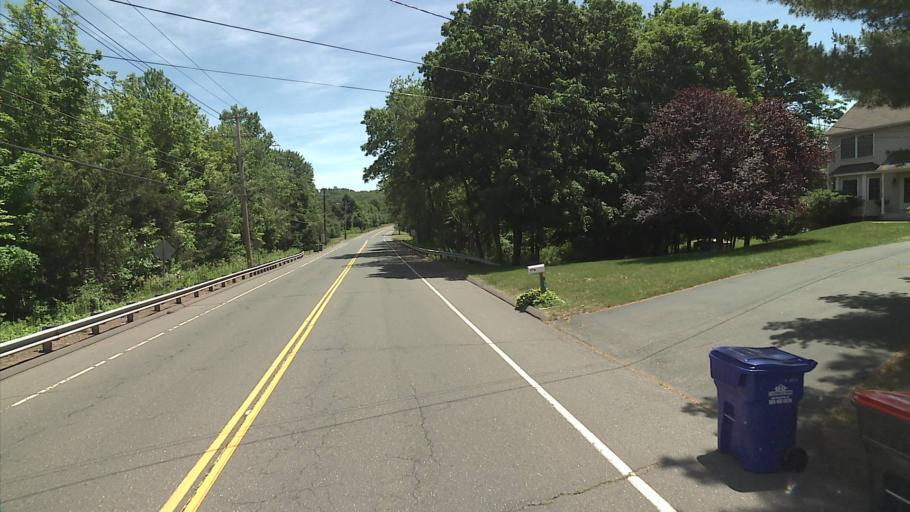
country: US
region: Connecticut
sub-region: New Haven County
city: Meriden
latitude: 41.5976
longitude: -72.8495
